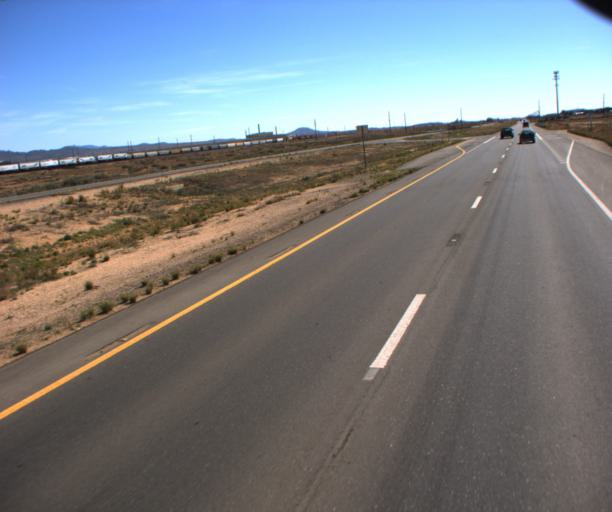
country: US
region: Arizona
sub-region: Mohave County
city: New Kingman-Butler
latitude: 35.2684
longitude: -113.9620
